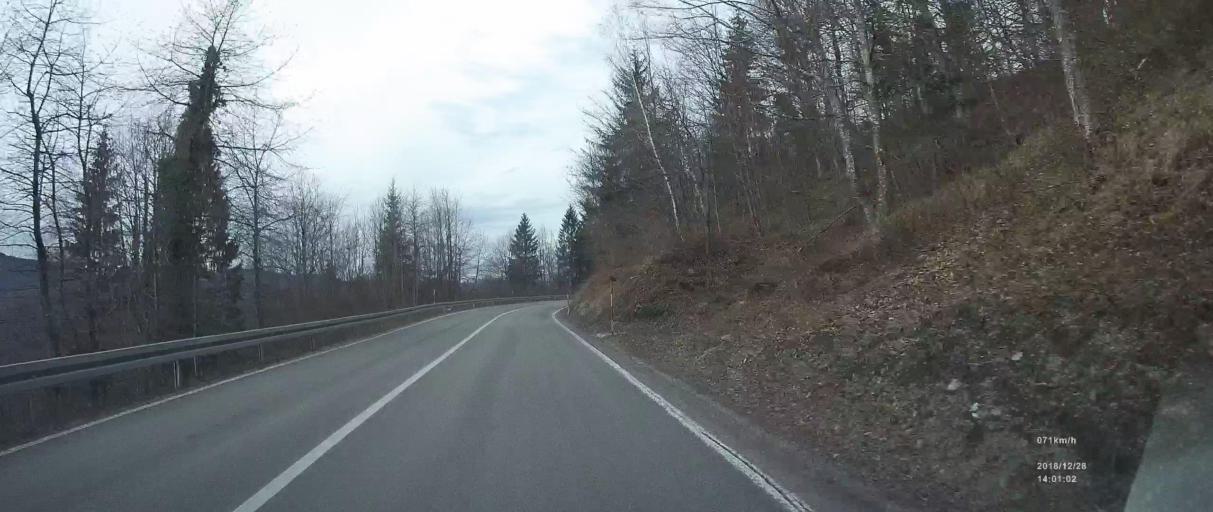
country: SI
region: Kostel
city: Kostel
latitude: 45.4167
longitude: 14.9109
